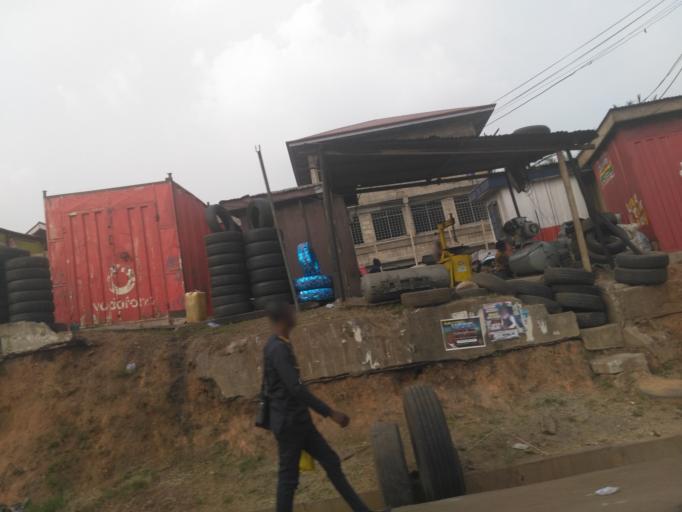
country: GH
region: Ashanti
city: Kumasi
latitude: 6.6870
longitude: -1.5748
